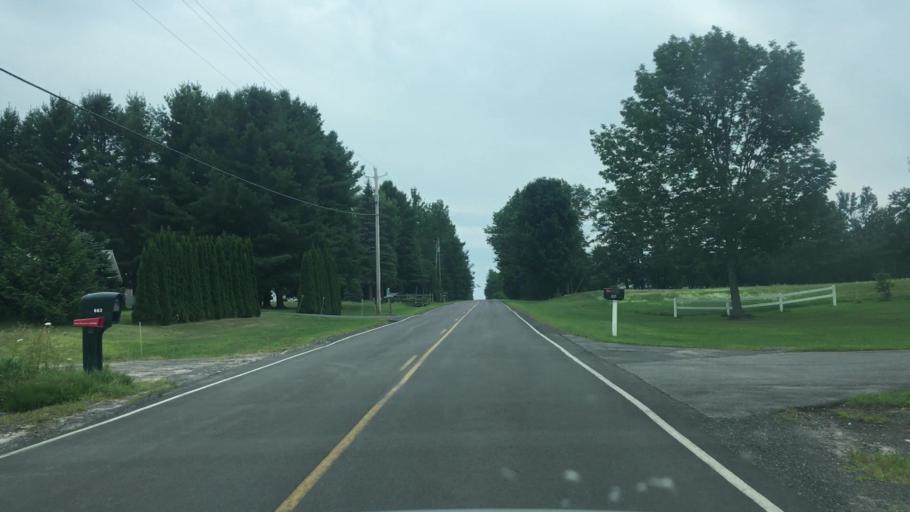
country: US
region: New York
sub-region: Clinton County
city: Peru
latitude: 44.6076
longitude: -73.6296
